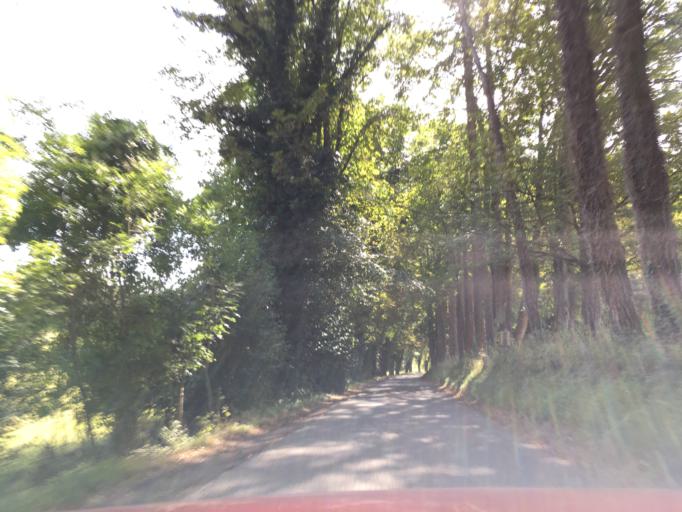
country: GB
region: England
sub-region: Hampshire
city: Highclere
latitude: 51.2779
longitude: -1.3507
